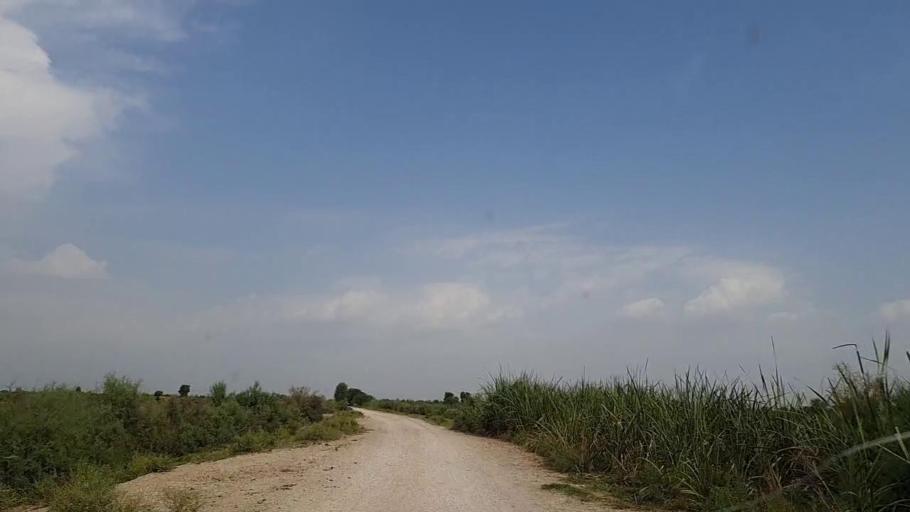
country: PK
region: Sindh
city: Khanpur
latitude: 27.8270
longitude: 69.5146
